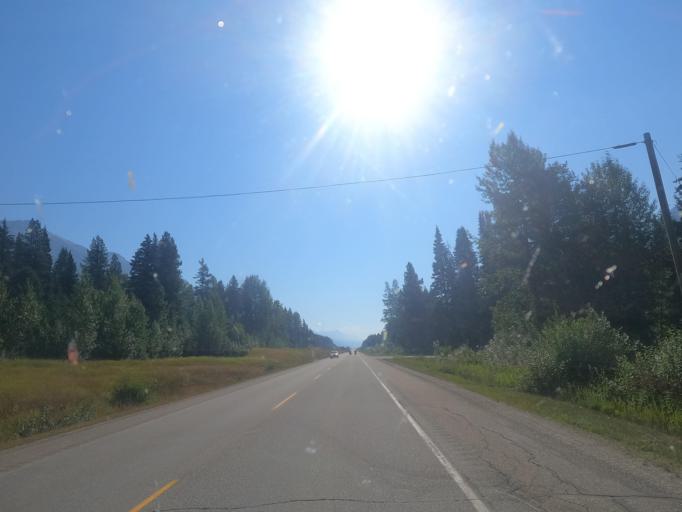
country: CA
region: Alberta
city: Grande Cache
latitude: 52.9883
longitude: -119.0030
